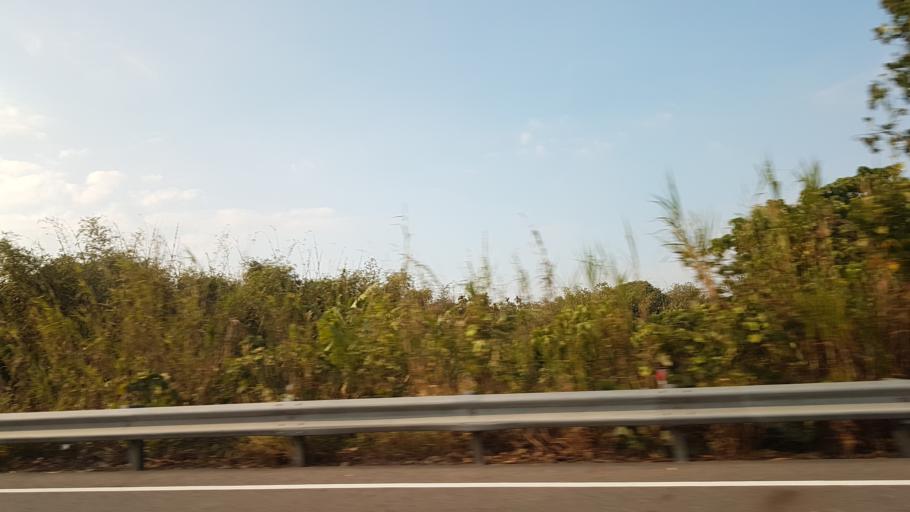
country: TW
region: Taiwan
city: Xinying
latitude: 23.3471
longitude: 120.4359
